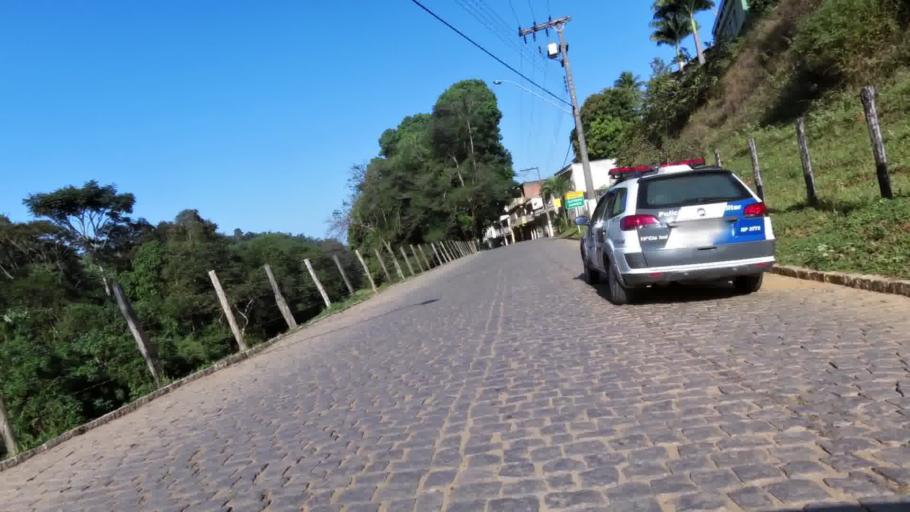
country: BR
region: Espirito Santo
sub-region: Alfredo Chaves
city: Alfredo Chaves
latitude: -20.6332
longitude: -40.7533
